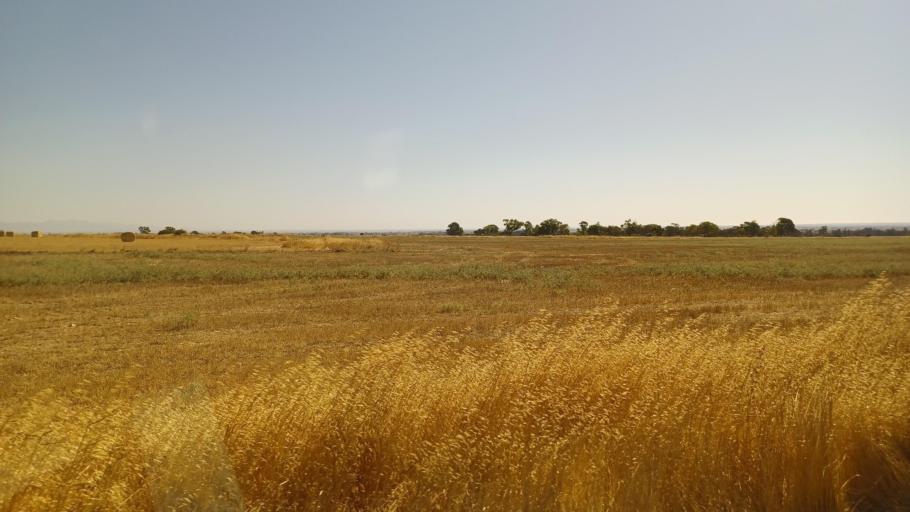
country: CY
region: Larnaka
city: Pergamos
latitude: 35.0413
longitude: 33.6857
